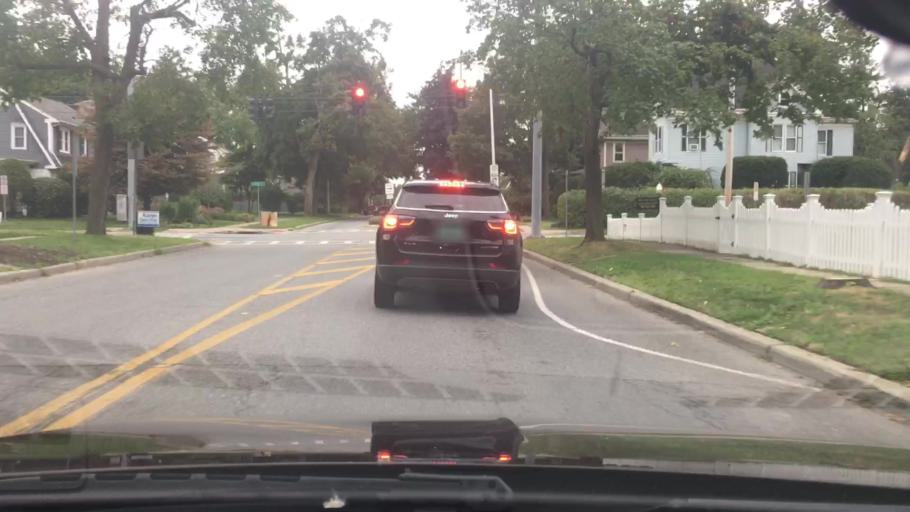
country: US
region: New York
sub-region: Dutchess County
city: Arlington
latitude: 41.6932
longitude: -73.9071
